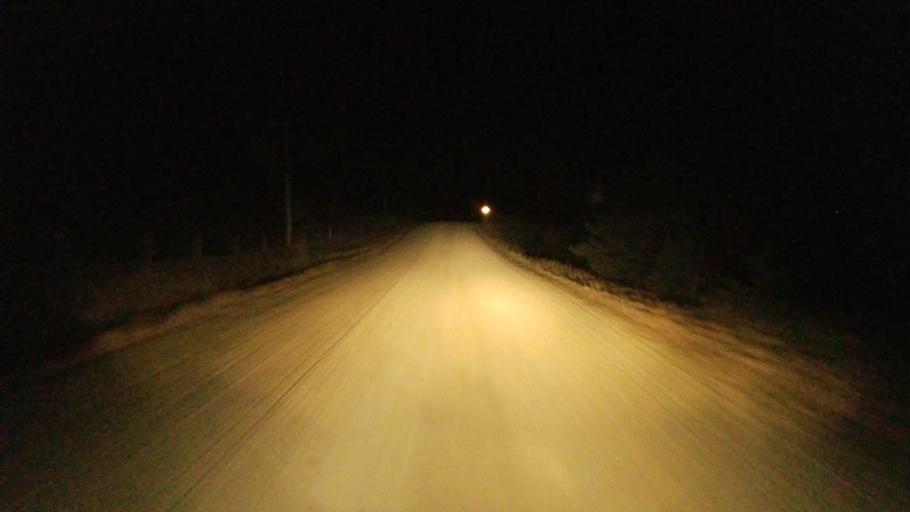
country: US
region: Nebraska
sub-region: Knox County
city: Center
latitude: 42.6220
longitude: -97.8379
